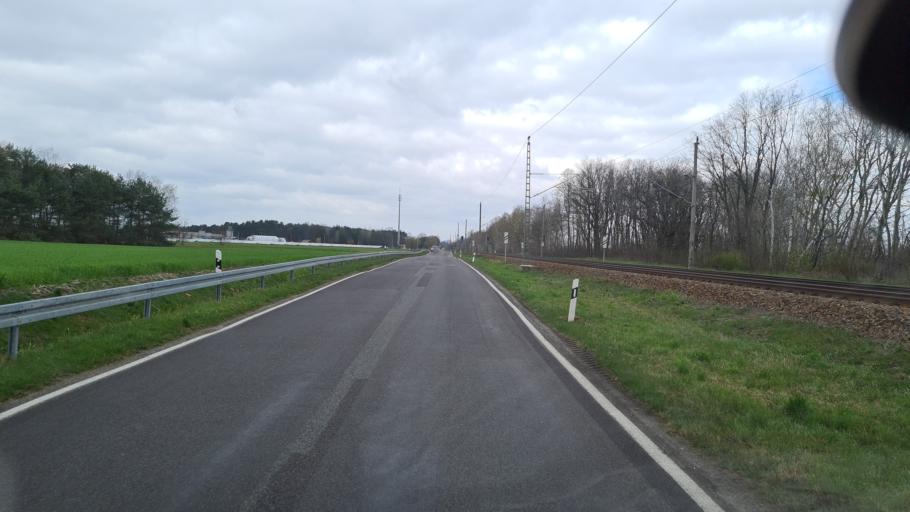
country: DE
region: Brandenburg
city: Ruhland
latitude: 51.4568
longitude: 13.8975
